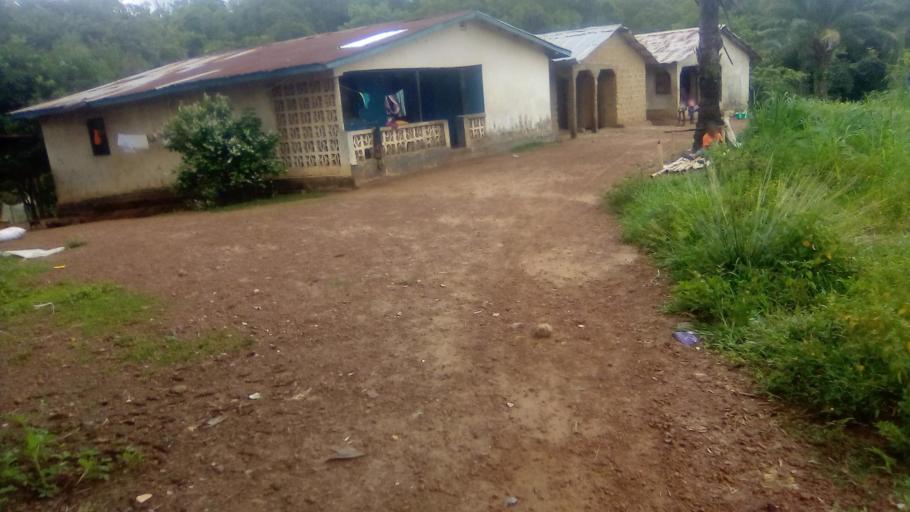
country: SL
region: Southern Province
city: Moyamba
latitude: 8.1557
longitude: -12.4257
